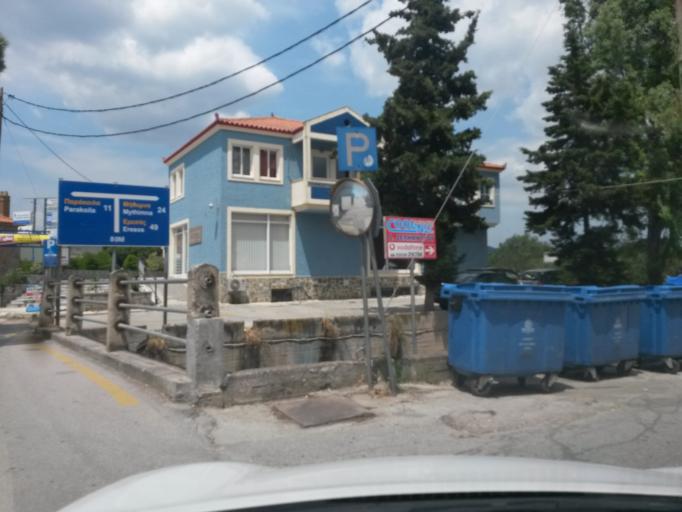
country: GR
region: North Aegean
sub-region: Nomos Lesvou
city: Kalloni
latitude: 39.2339
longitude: 26.2086
